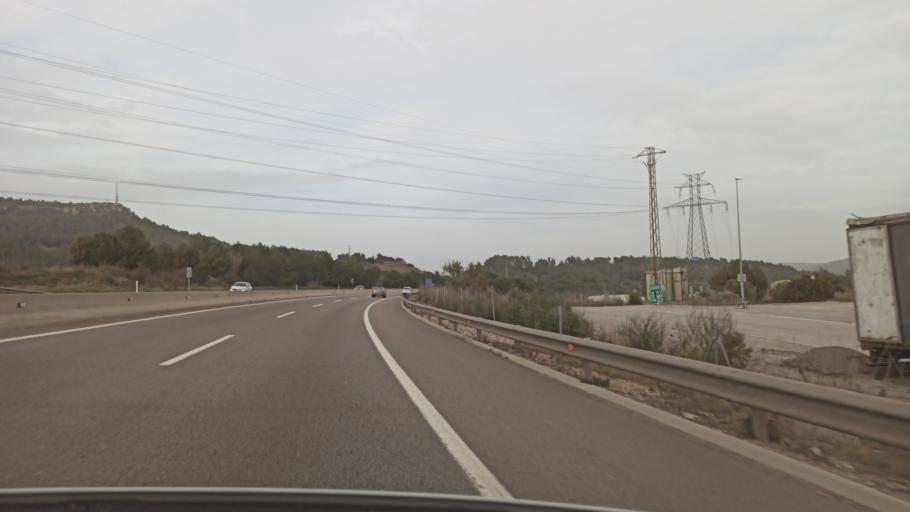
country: ES
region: Catalonia
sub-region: Provincia de Barcelona
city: Palleja
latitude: 41.4044
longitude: 1.9867
